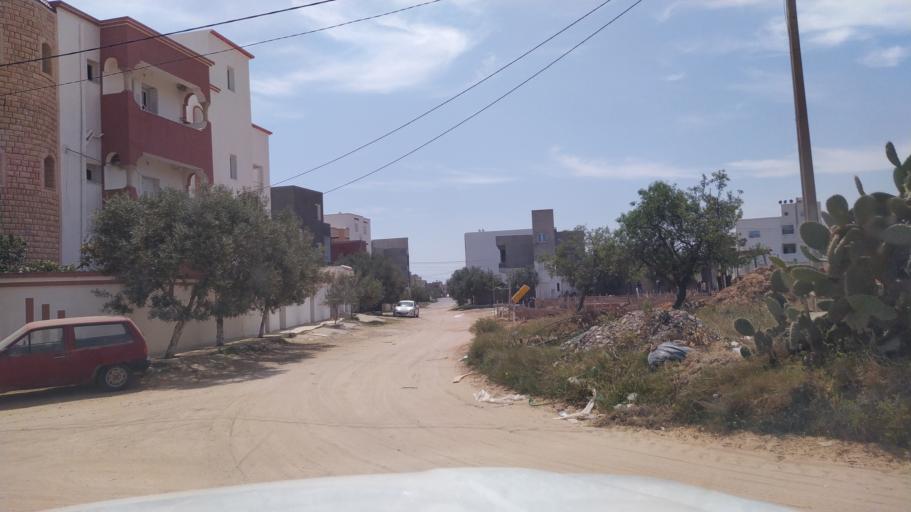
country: TN
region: Al Mahdiyah
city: Zouila
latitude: 35.5038
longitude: 11.0356
